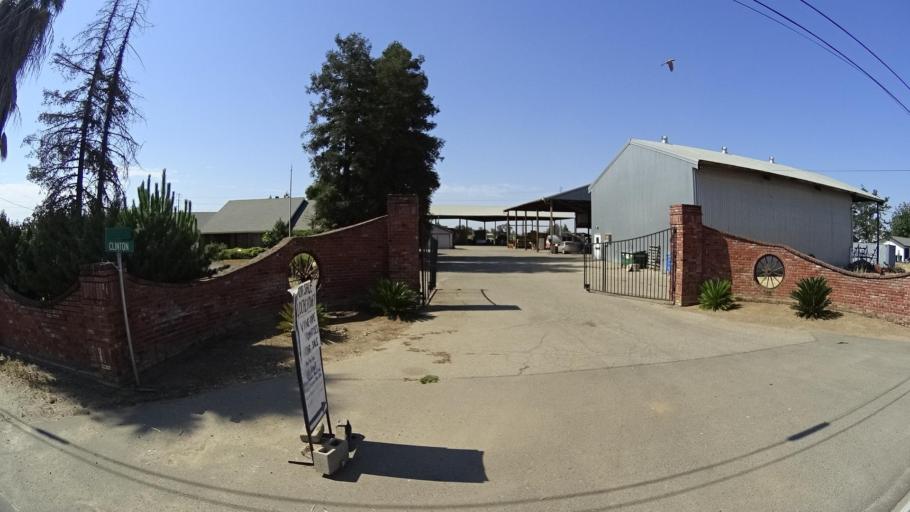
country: US
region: California
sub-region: Fresno County
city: Tarpey Village
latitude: 36.7721
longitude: -119.6759
